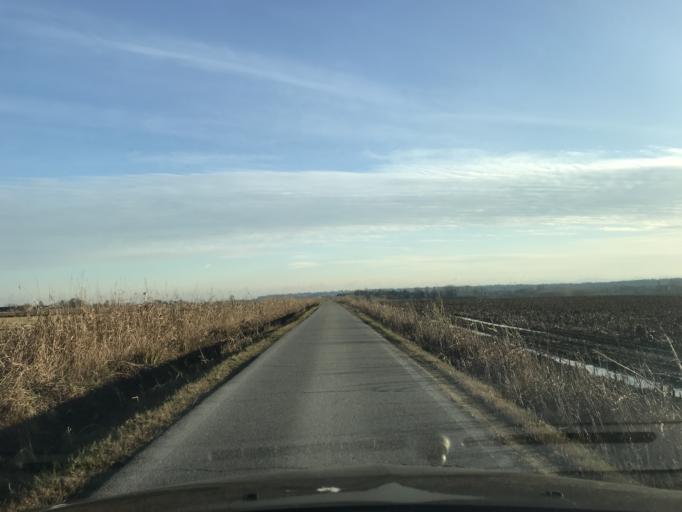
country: IT
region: Lombardy
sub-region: Provincia di Lodi
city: Bargano
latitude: 45.2278
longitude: 9.4592
